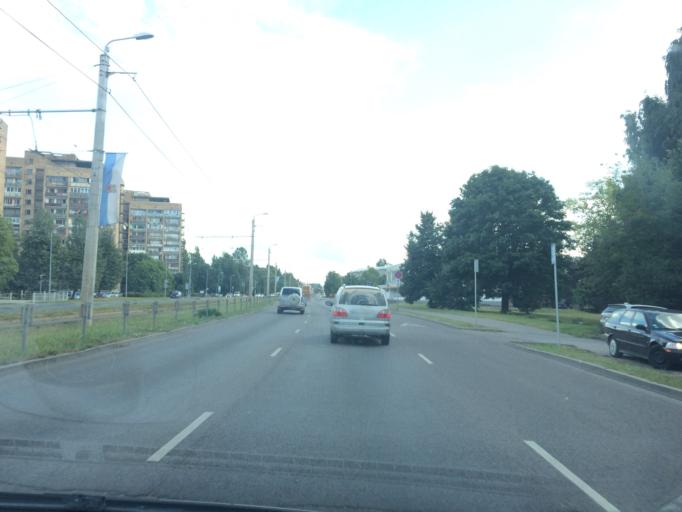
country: LV
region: Kekava
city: Balozi
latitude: 56.9096
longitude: 24.1806
